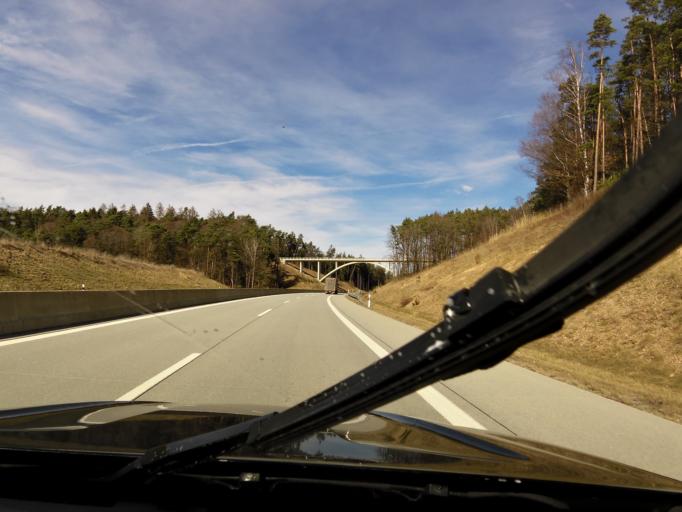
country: DE
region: Bavaria
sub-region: Upper Palatinate
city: Schierling
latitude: 48.7633
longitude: 12.1334
